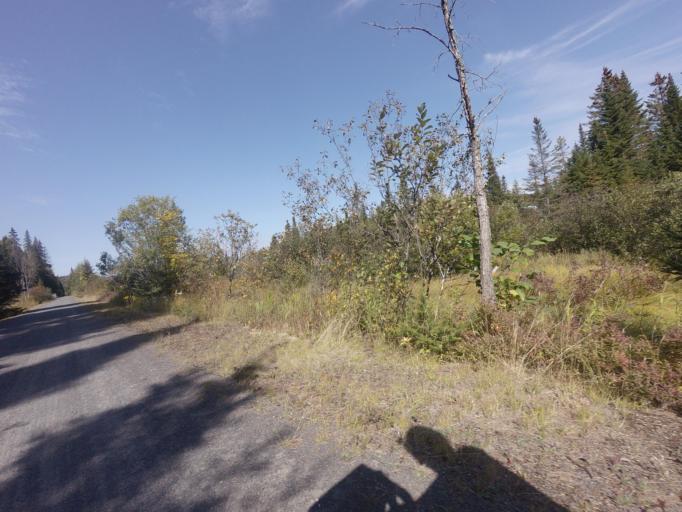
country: CA
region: Quebec
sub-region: Laurentides
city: Sainte-Agathe-des-Monts
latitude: 46.0618
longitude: -74.3009
